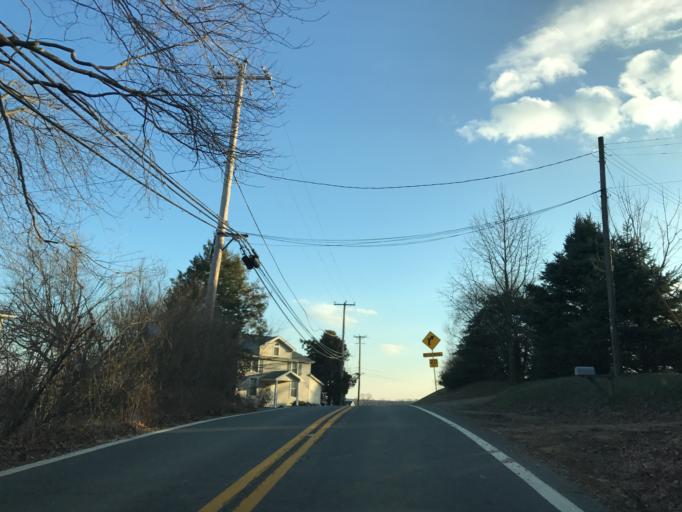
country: US
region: Maryland
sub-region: Cecil County
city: Charlestown
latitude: 39.5137
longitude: -75.9518
